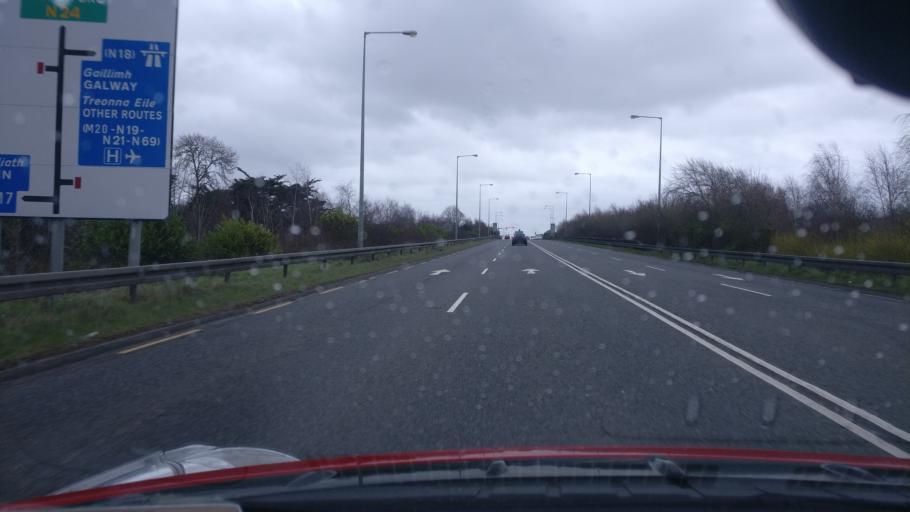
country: IE
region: Munster
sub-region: County Limerick
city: Annacotty
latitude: 52.6491
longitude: -8.5698
